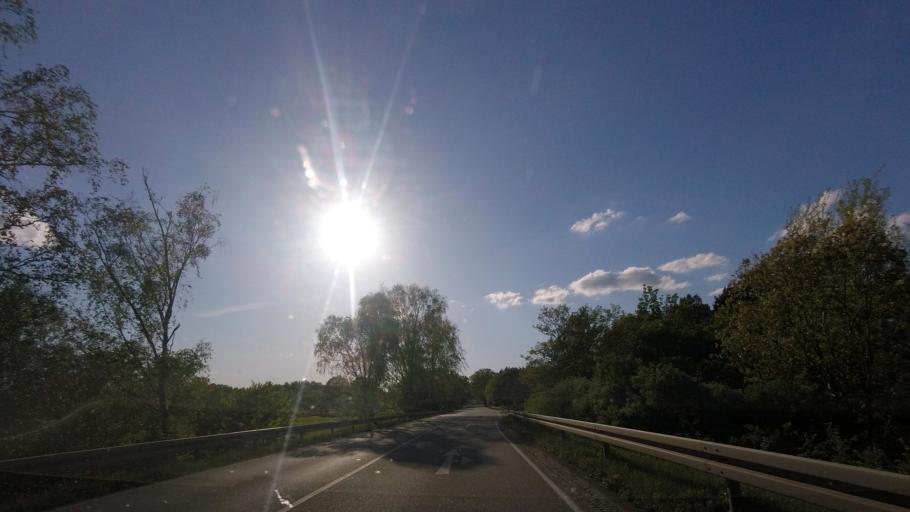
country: DE
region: Brandenburg
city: Kasel-Golzig
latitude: 51.9543
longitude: 13.7651
